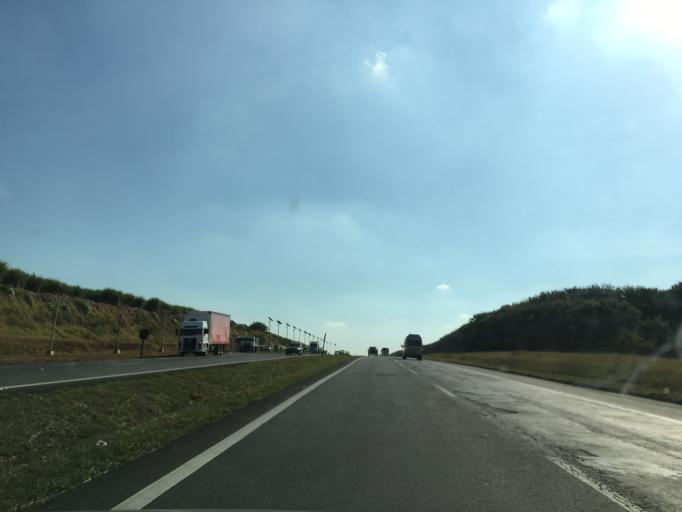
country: BR
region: Sao Paulo
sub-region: Piracicaba
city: Piracicaba
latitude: -22.7257
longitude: -47.5672
